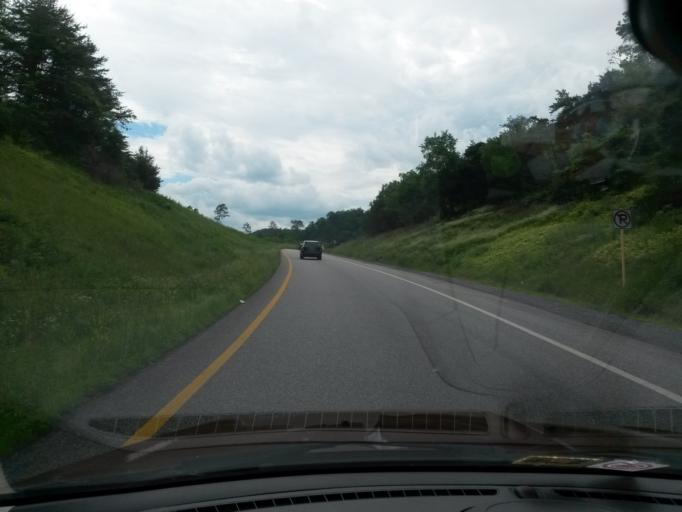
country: US
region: Virginia
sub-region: Alleghany County
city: Clifton Forge
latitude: 37.8280
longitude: -79.7942
